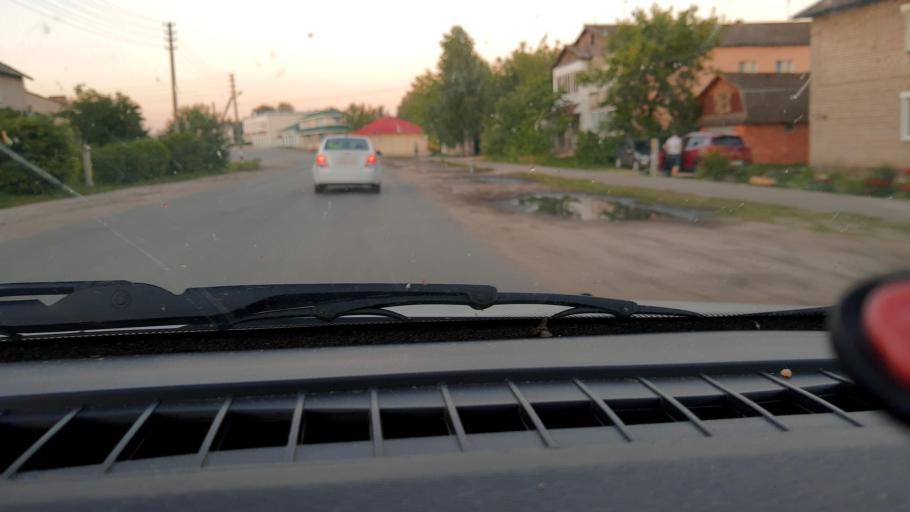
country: RU
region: Nizjnij Novgorod
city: Uren'
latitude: 57.4542
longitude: 45.7874
